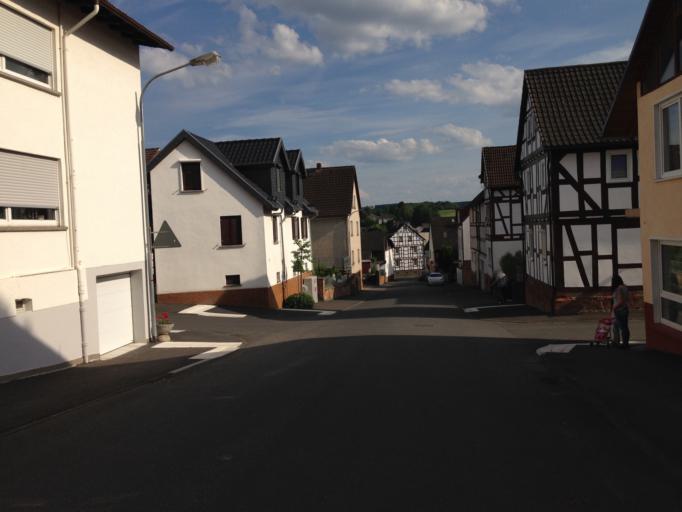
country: DE
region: Hesse
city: Staufenberg
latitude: 50.6629
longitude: 8.7451
